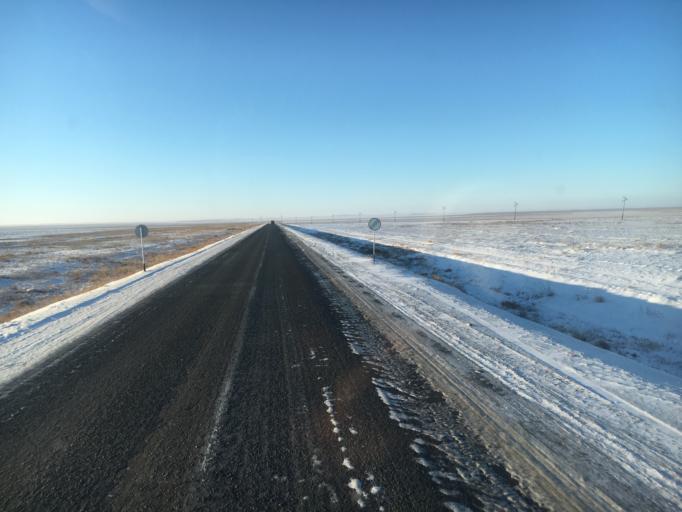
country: KZ
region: Aqtoebe
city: Khromtau
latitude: 50.1186
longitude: 58.9232
